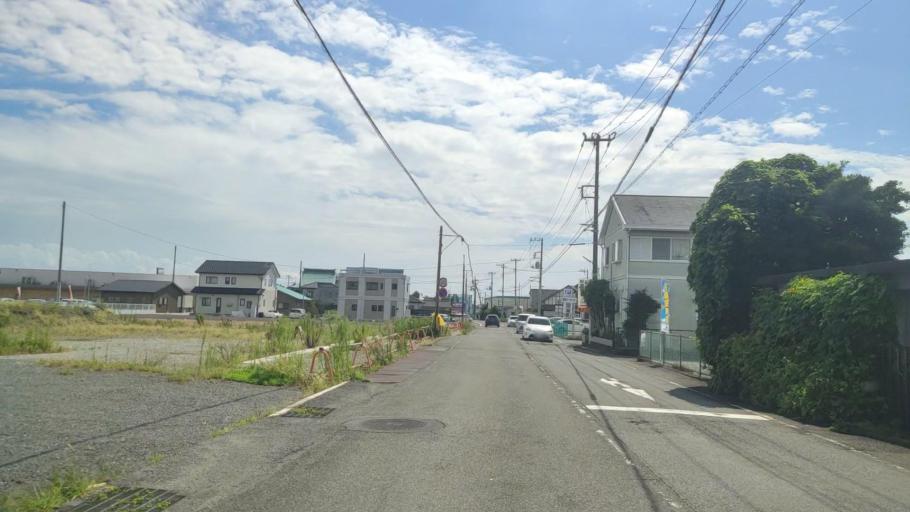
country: JP
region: Shizuoka
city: Fuji
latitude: 35.1407
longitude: 138.6636
